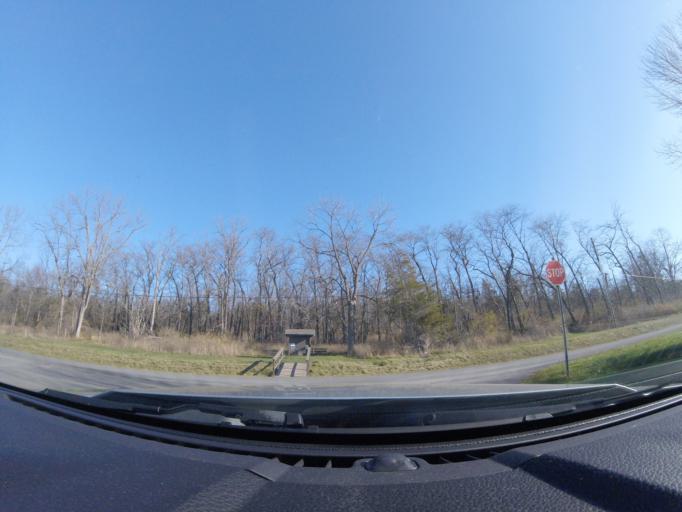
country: US
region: New York
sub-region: Cayuga County
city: Union Springs
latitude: 42.7165
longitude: -76.7072
